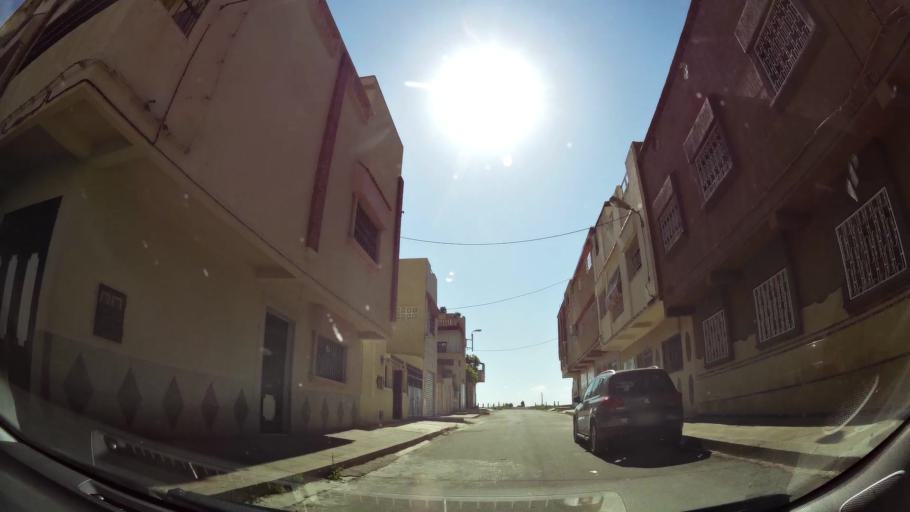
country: MA
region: Oriental
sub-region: Oujda-Angad
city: Oujda
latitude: 34.6941
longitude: -1.9216
